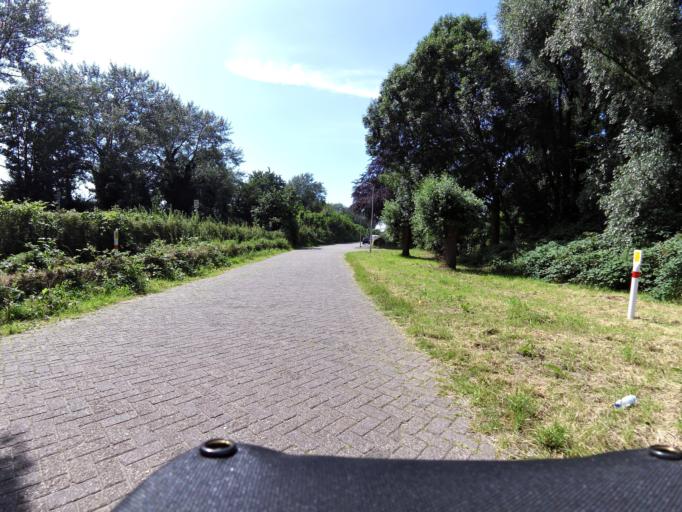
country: NL
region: South Holland
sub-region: Gemeente Albrandswaard
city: Rhoon
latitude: 51.8616
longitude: 4.3854
